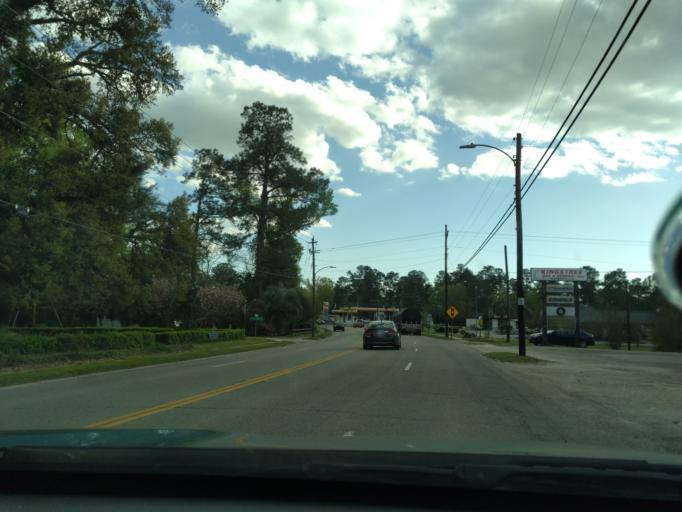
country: US
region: South Carolina
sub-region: Williamsburg County
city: Kingstree
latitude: 33.6730
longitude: -79.8357
